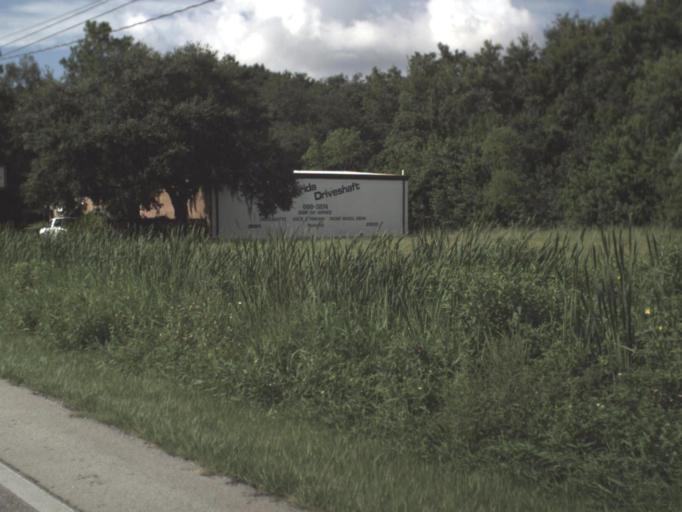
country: US
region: Florida
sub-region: Polk County
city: Crystal Lake
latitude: 28.0422
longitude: -81.9080
